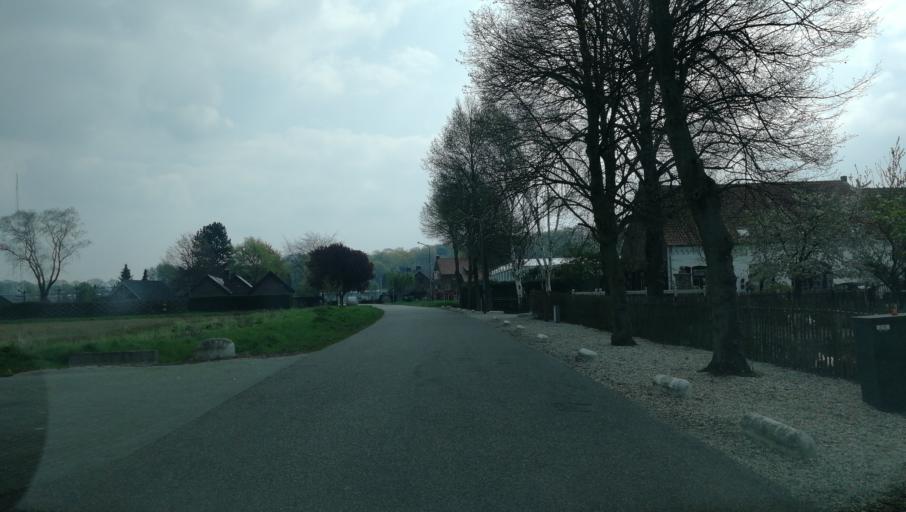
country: NL
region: Limburg
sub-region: Gemeente Venlo
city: Venlo
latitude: 51.3850
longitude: 6.2041
